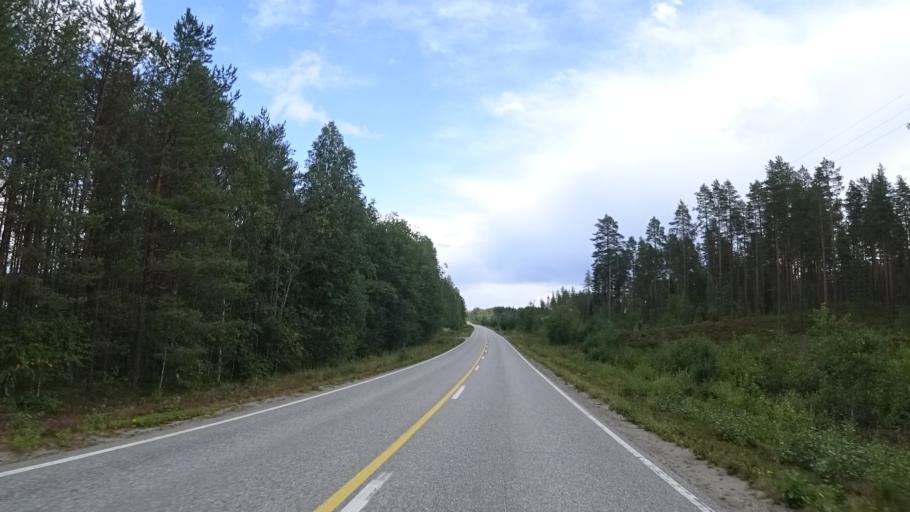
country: FI
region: North Karelia
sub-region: Joensuu
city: Ilomantsi
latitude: 62.6438
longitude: 31.0404
